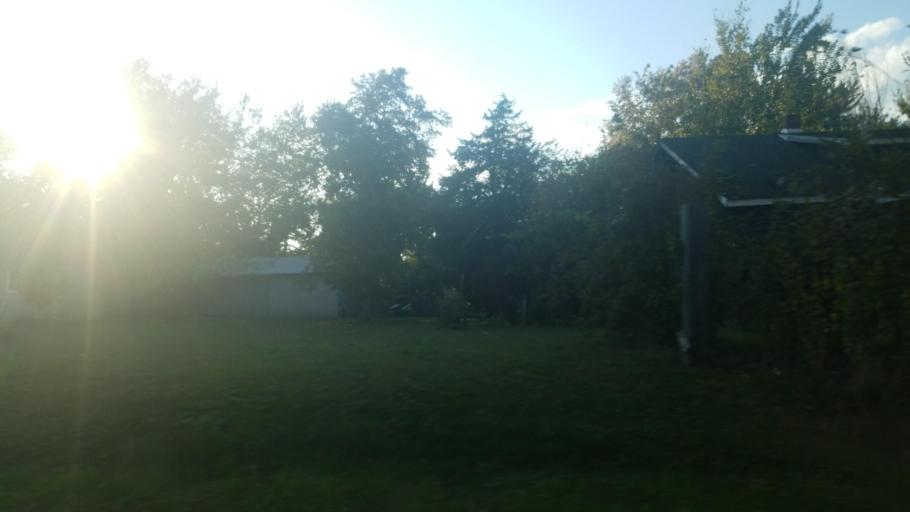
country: US
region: Illinois
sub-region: Williamson County
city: Marion
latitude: 37.7620
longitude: -88.8059
